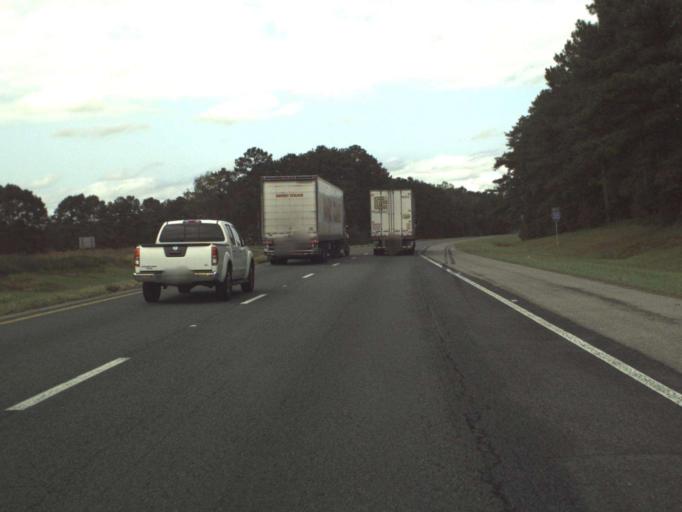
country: US
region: Florida
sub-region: Gadsden County
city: Gretna
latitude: 30.5806
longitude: -84.7062
